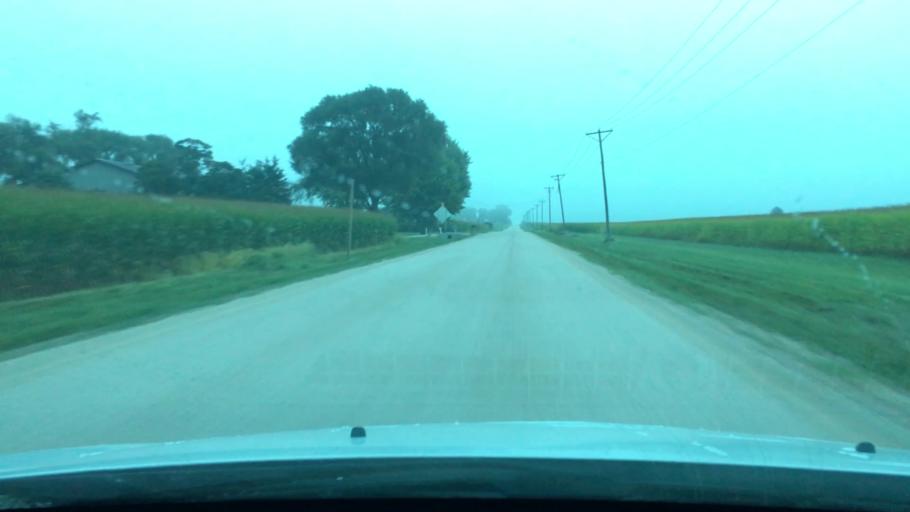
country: US
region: Illinois
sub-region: Ogle County
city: Rochelle
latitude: 41.9200
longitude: -89.0167
